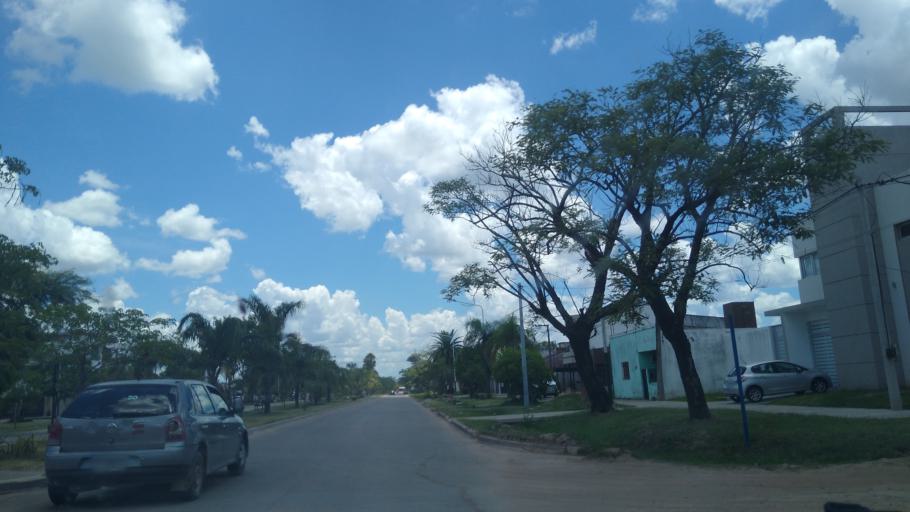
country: AR
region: Chaco
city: Presidencia Roque Saenz Pena
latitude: -26.7757
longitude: -60.4392
